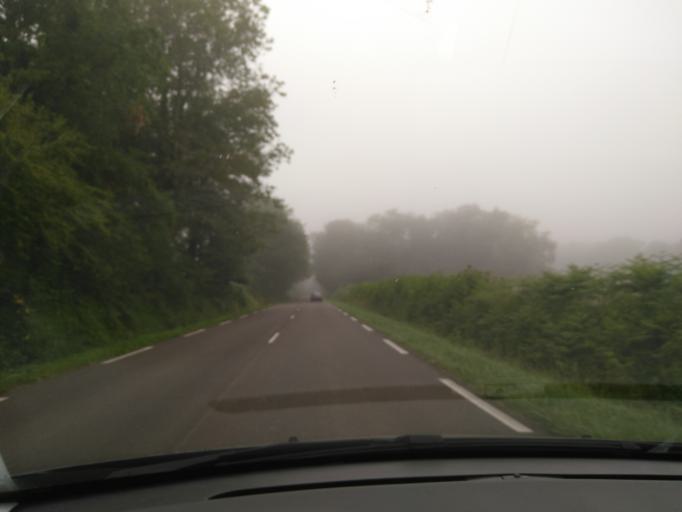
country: FR
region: Aquitaine
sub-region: Departement des Landes
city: Mont-de-Marsan
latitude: 43.8886
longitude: -0.4329
